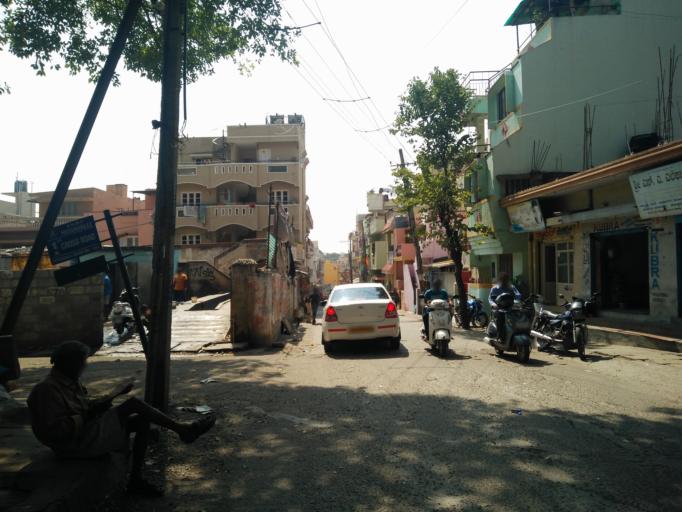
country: IN
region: Karnataka
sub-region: Bangalore Urban
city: Bangalore
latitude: 12.9704
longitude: 77.5422
